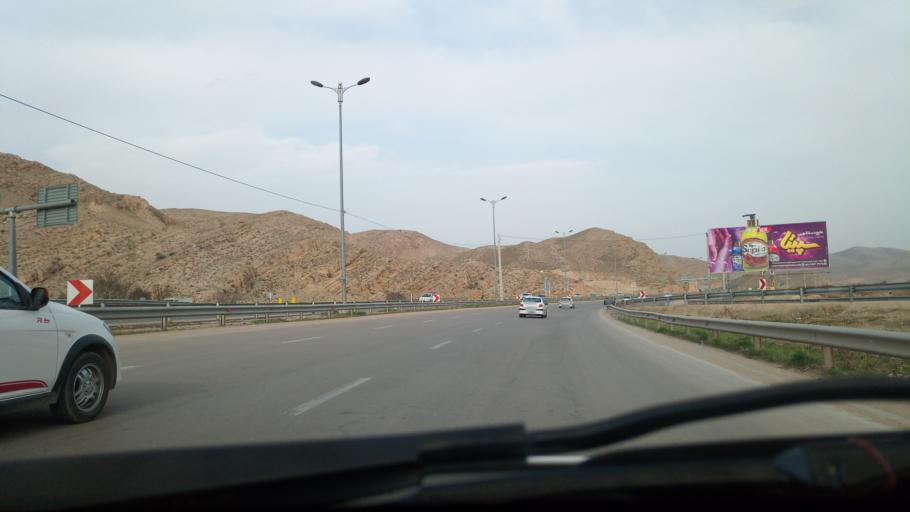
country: IR
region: Khorasan-e Shomali
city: Bojnurd
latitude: 37.4809
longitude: 57.3992
